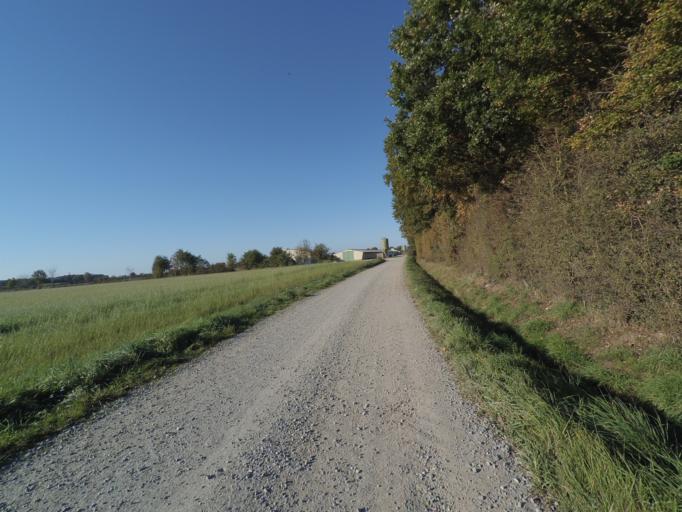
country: FR
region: Pays de la Loire
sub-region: Departement de la Loire-Atlantique
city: Remouille
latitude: 47.0113
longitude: -1.3839
